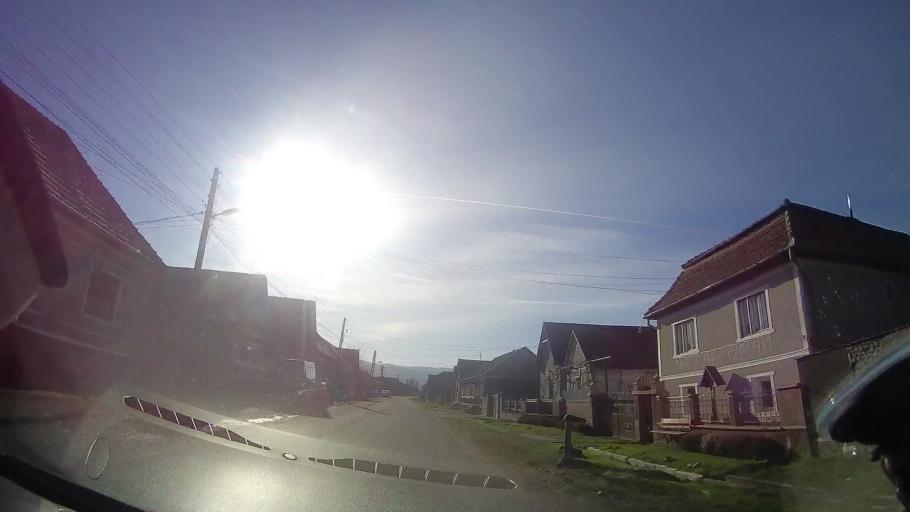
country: RO
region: Bihor
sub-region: Comuna Magesti
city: Magesti
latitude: 47.0231
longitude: 22.4713
